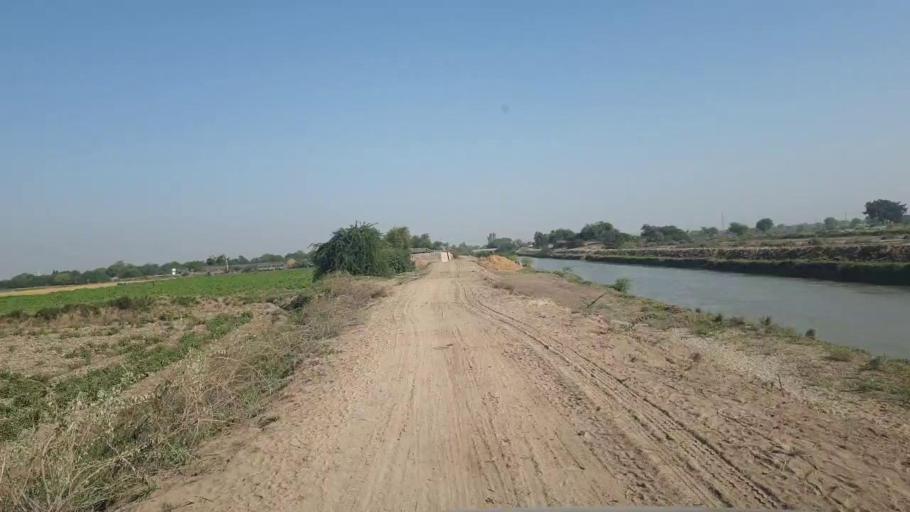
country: PK
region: Sindh
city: Badin
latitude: 24.7280
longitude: 68.8045
